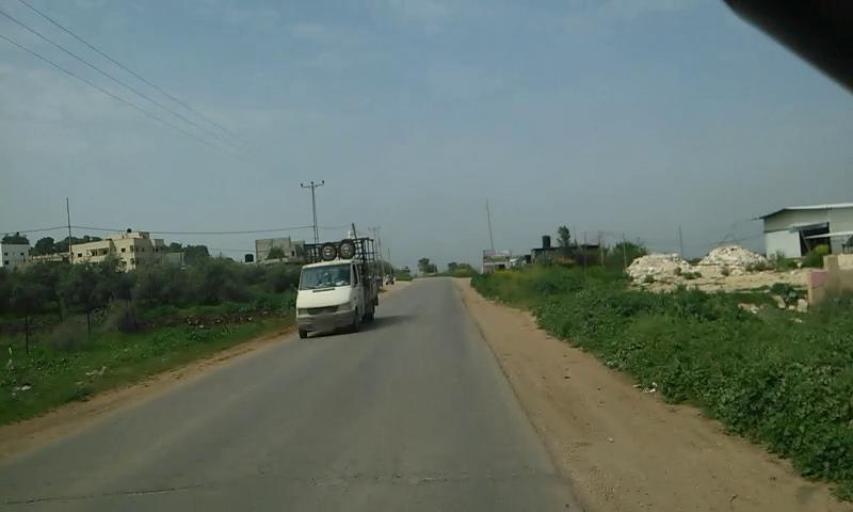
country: PS
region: West Bank
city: Kafr Dan
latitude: 32.4944
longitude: 35.2557
